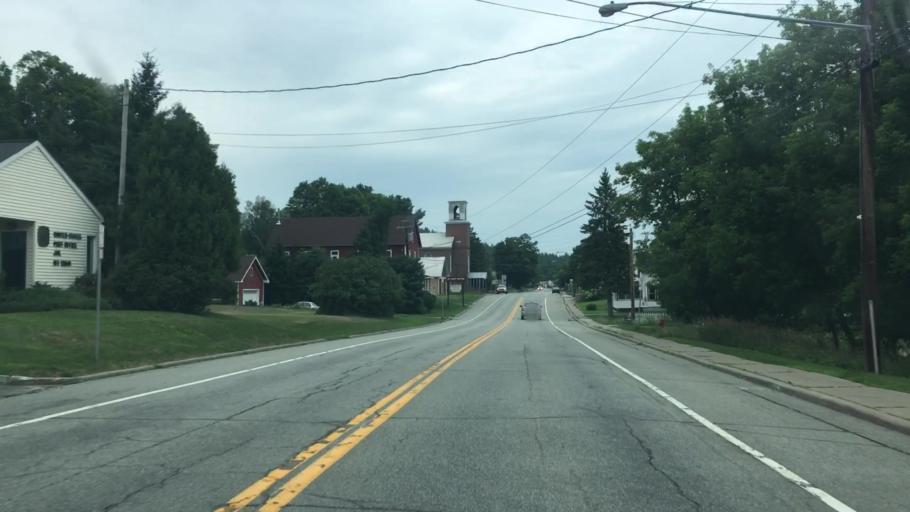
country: US
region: New York
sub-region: Essex County
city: Elizabethtown
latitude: 44.3736
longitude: -73.7295
